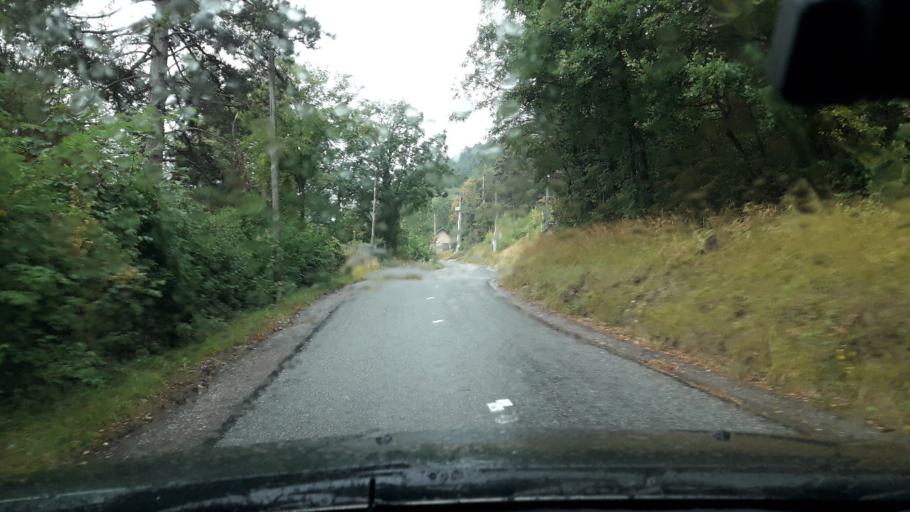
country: FR
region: Rhone-Alpes
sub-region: Departement de la Savoie
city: Saint-Baldoph
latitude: 45.5359
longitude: 5.9400
